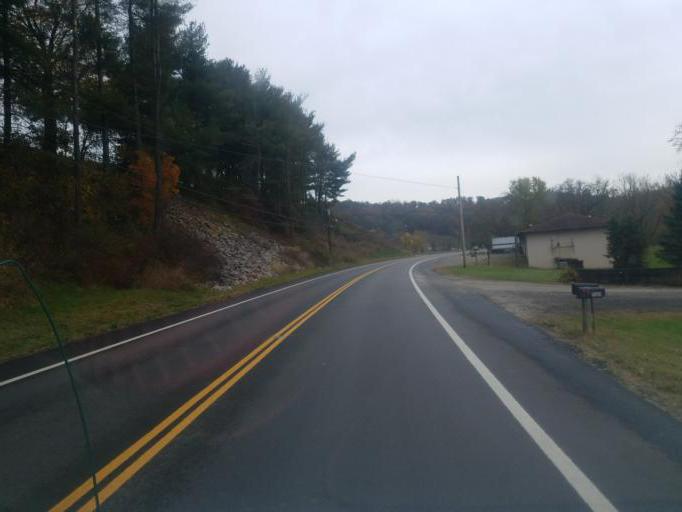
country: US
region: Ohio
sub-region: Washington County
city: Devola
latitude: 39.5334
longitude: -81.5205
